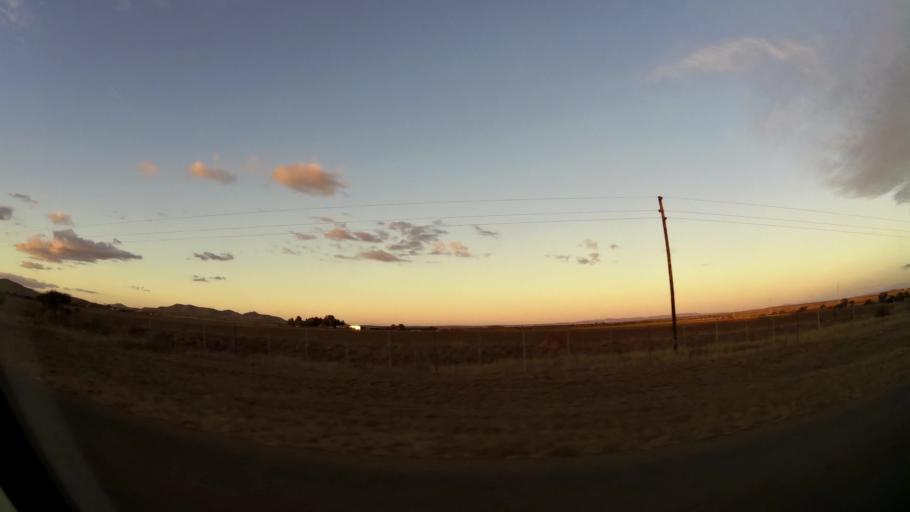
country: ZA
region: Limpopo
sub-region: Capricorn District Municipality
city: Polokwane
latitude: -23.7480
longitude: 29.4713
